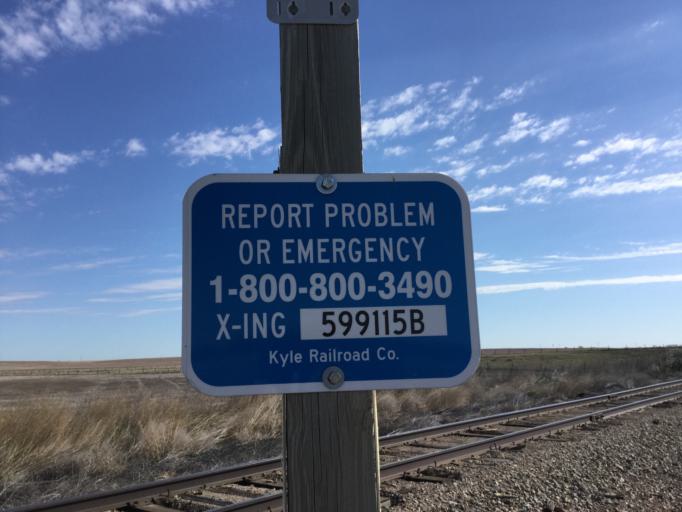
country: US
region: Kansas
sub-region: Norton County
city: Norton
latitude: 39.7264
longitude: -100.2056
